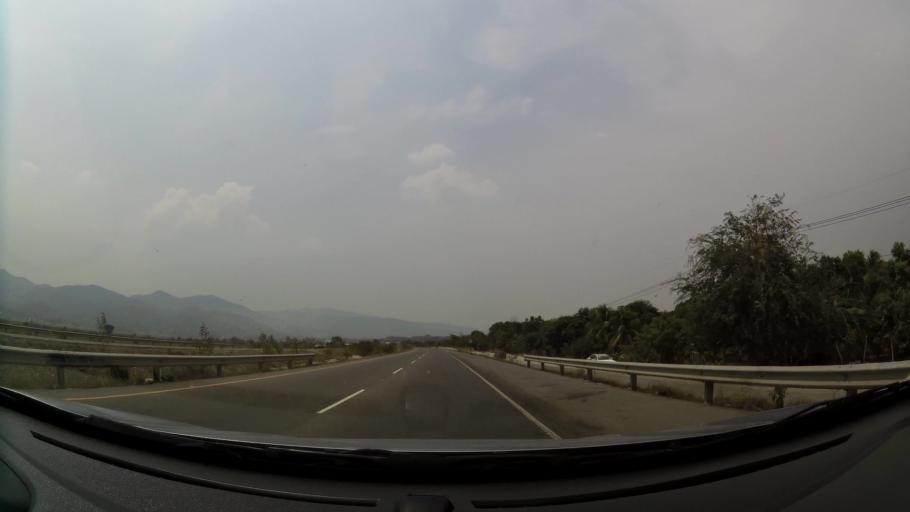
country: HN
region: Cortes
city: El Plan
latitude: 15.2923
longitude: -87.9784
